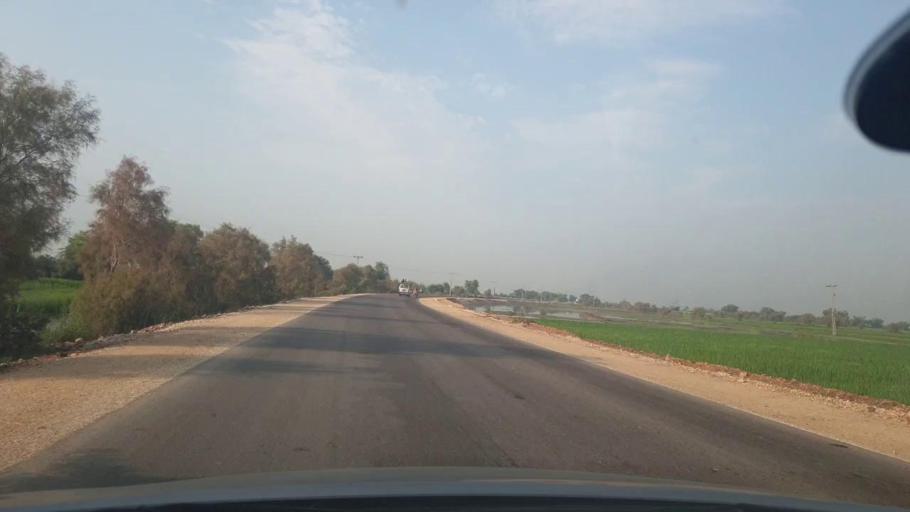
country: PK
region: Sindh
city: Jacobabad
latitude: 28.2393
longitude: 68.3919
